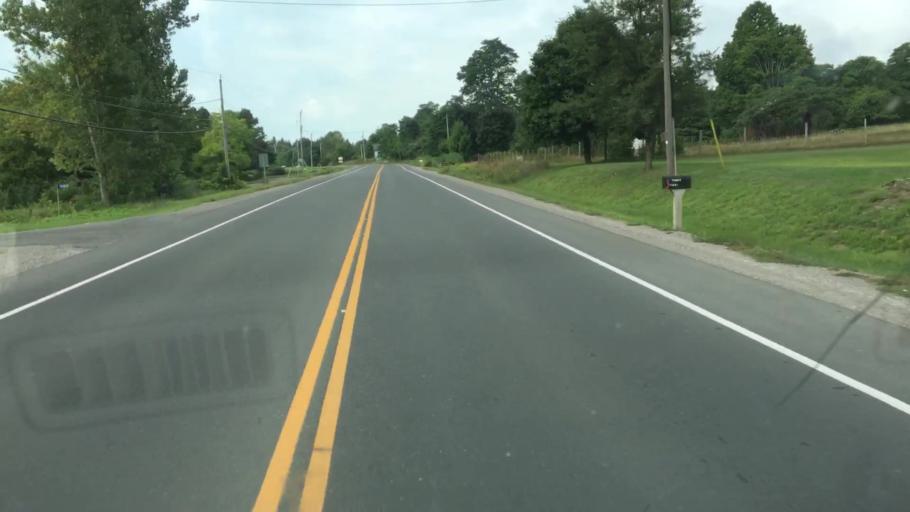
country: CA
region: Ontario
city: Quinte West
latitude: 44.0282
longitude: -77.7803
